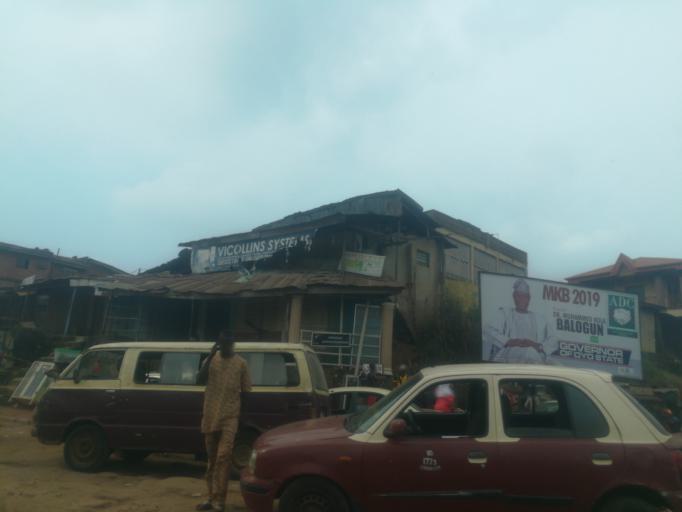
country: NG
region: Oyo
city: Ibadan
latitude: 7.4039
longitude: 3.9425
